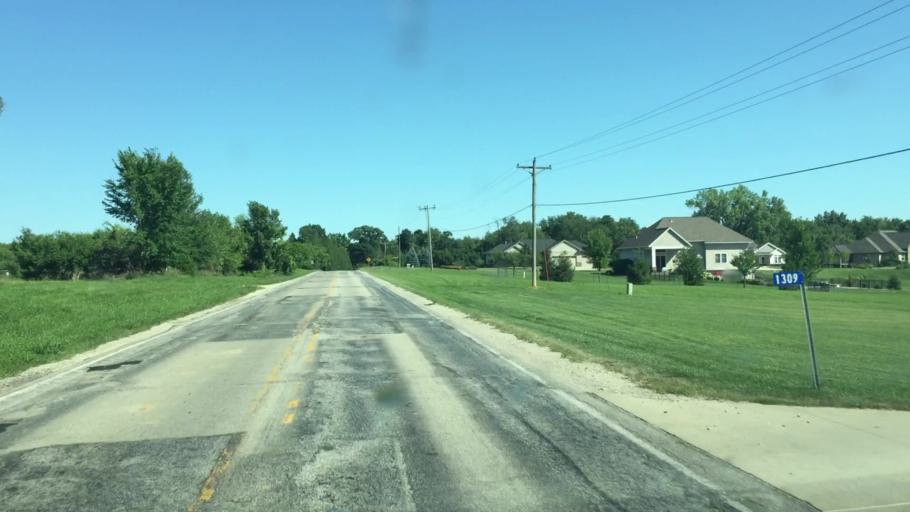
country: US
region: Iowa
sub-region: Linn County
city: Ely
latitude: 41.8395
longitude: -91.6402
